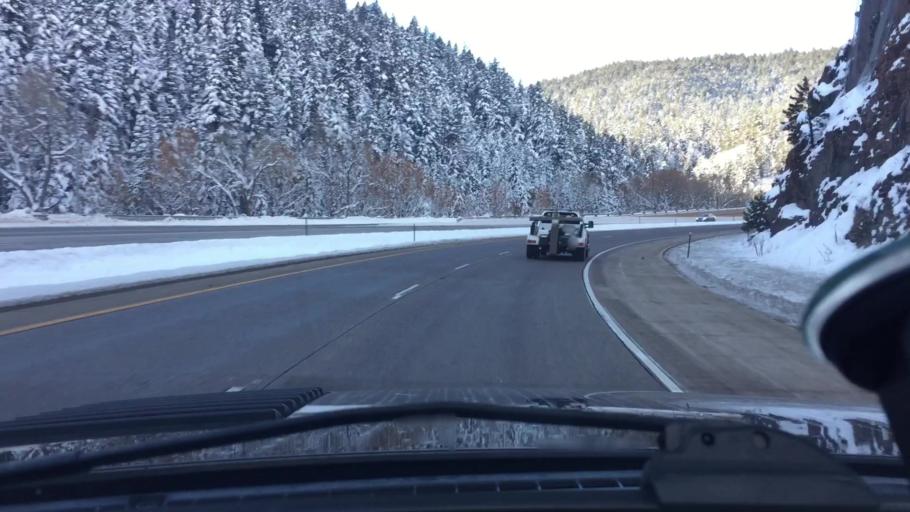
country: US
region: Colorado
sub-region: Jefferson County
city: Indian Hills
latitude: 39.6175
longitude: -105.2293
